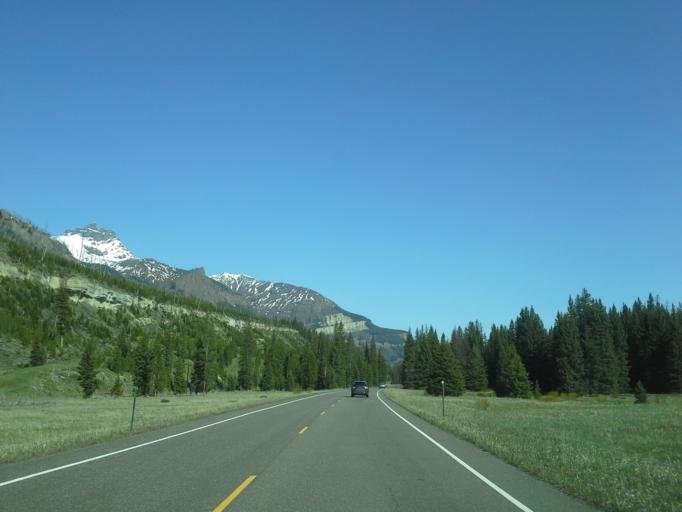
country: US
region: Montana
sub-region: Carbon County
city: Red Lodge
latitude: 44.9633
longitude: -109.8218
